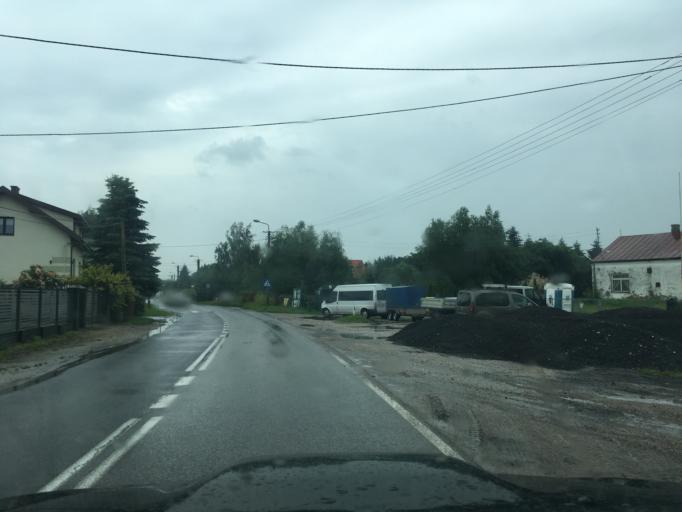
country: PL
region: Masovian Voivodeship
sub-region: Powiat piaseczynski
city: Gora Kalwaria
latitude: 51.9813
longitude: 21.2628
